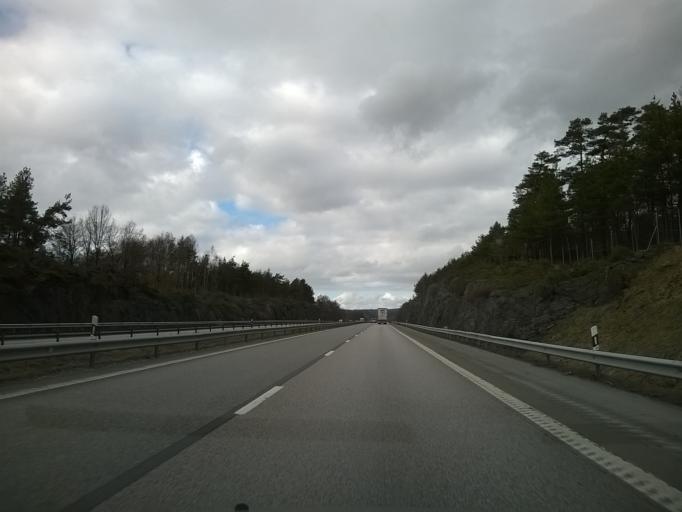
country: SE
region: Halland
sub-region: Varbergs Kommun
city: Veddige
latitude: 57.2115
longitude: 12.2411
